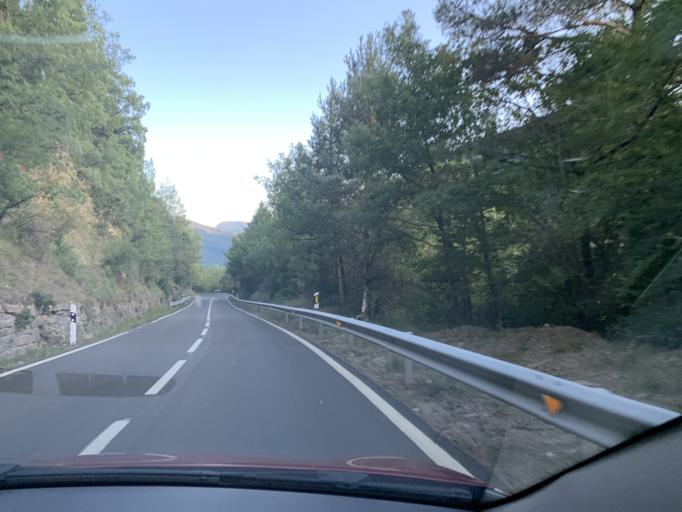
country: ES
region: Aragon
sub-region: Provincia de Huesca
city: Broto
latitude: 42.5924
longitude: -0.1185
